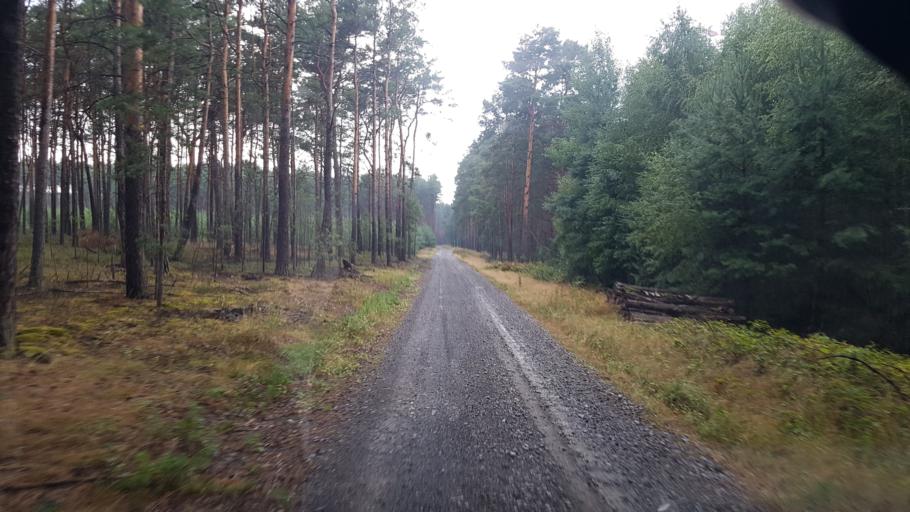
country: DE
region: Brandenburg
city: Sallgast
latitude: 51.6297
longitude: 13.7987
